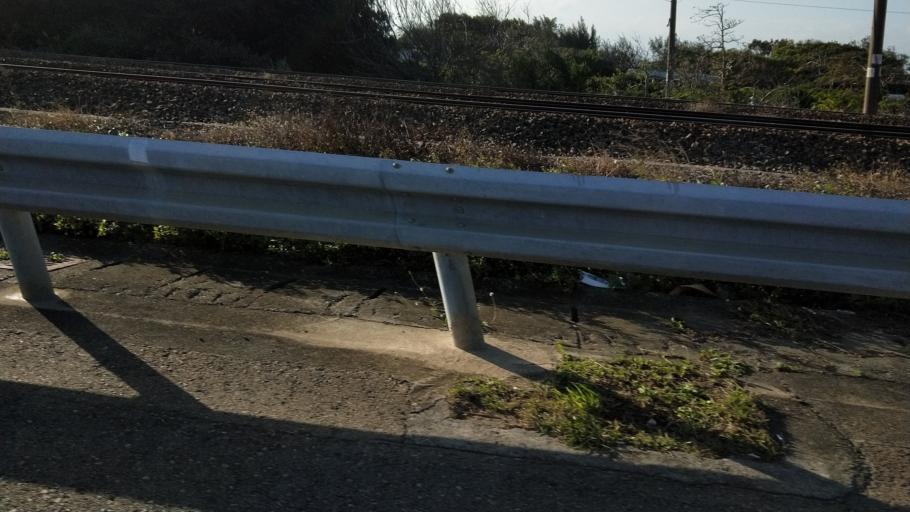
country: TW
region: Taiwan
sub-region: Miaoli
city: Miaoli
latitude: 24.5361
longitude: 120.6946
